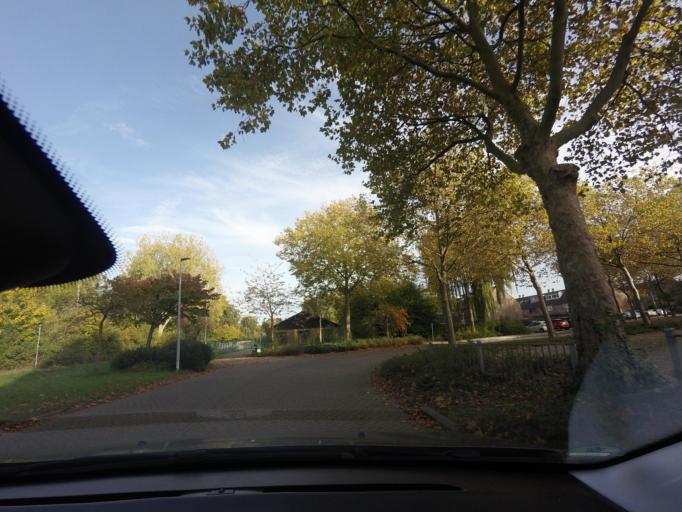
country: NL
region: South Holland
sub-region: Gemeente Spijkenisse
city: Spijkenisse
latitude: 51.8615
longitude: 4.3725
